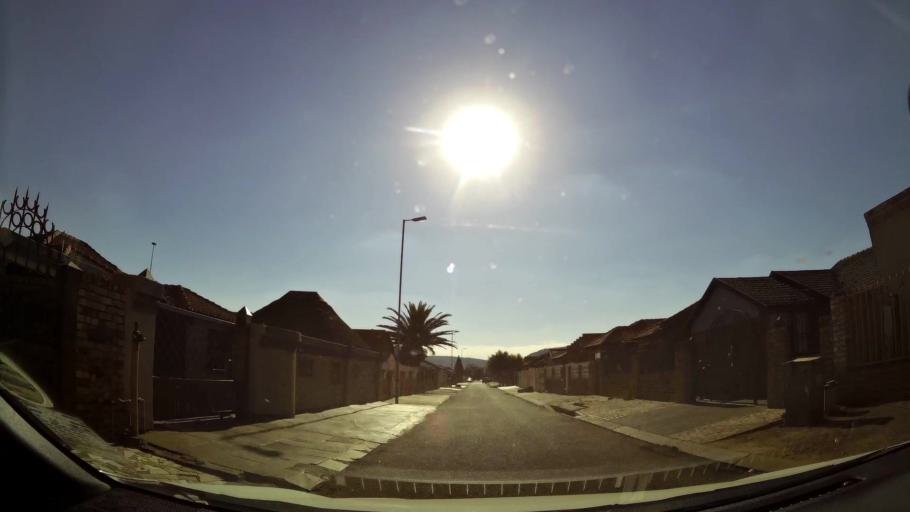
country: ZA
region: Gauteng
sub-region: City of Tshwane Metropolitan Municipality
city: Cullinan
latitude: -25.7192
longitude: 28.3779
